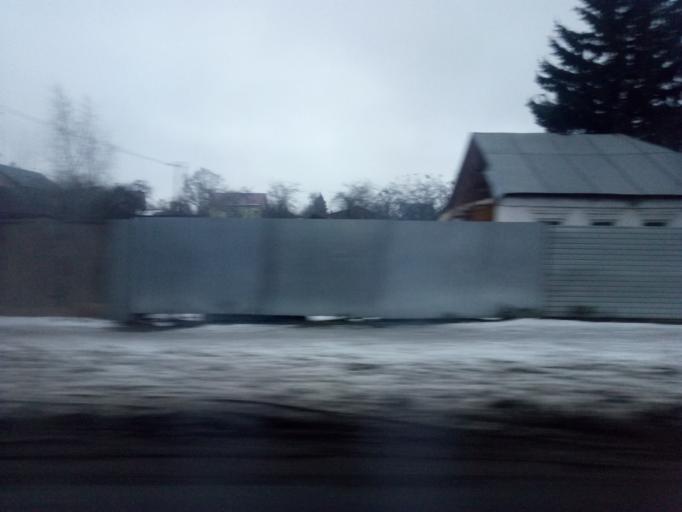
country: RU
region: Tula
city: Tula
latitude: 54.1993
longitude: 37.5594
